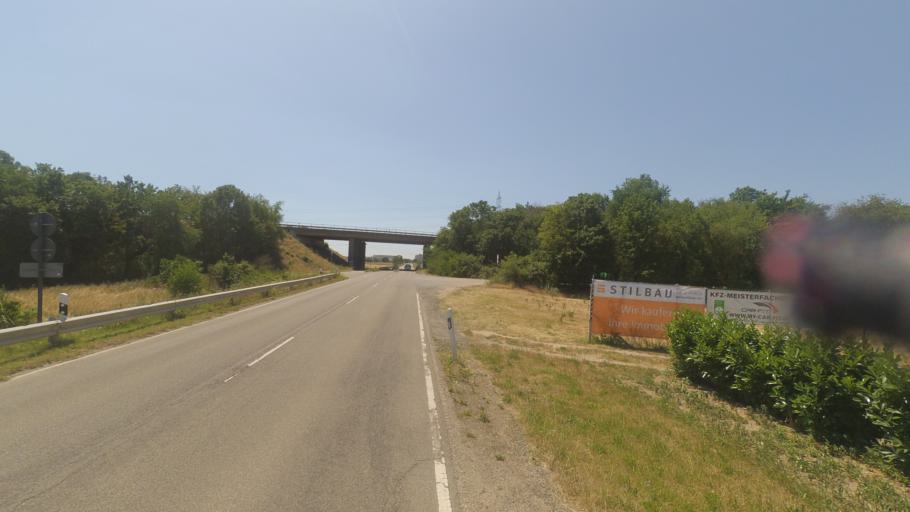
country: DE
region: Rheinland-Pfalz
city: Limburgerhof
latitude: 49.4352
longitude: 8.4010
